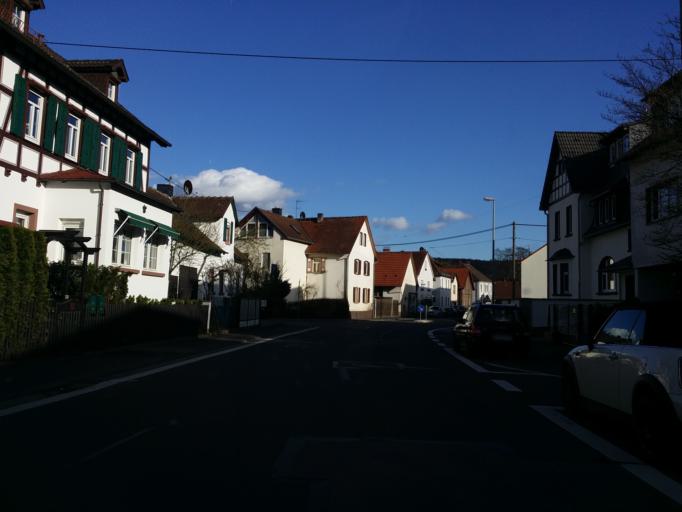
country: DE
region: Hesse
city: Kelkheim (Taunus)
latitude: 50.1185
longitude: 8.4196
